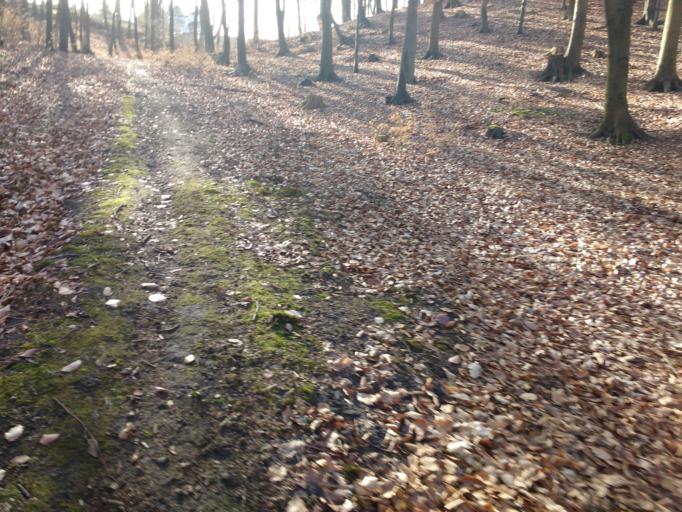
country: PL
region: Pomeranian Voivodeship
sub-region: Gdynia
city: Wielki Kack
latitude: 54.4784
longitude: 18.5149
